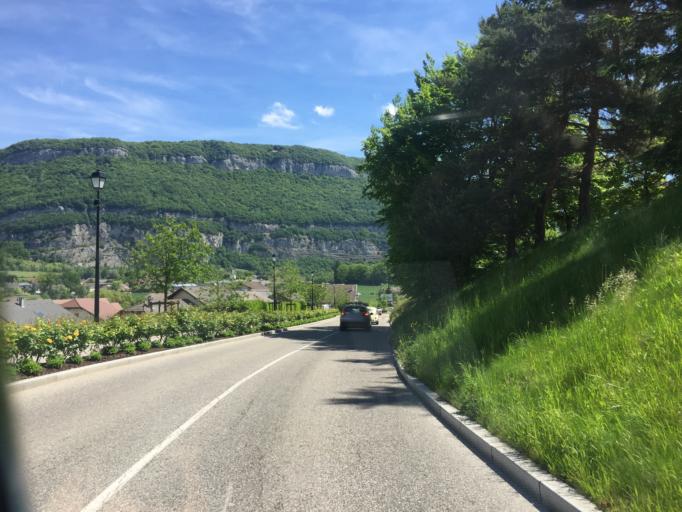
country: FR
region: Rhone-Alpes
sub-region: Departement de la Haute-Savoie
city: Sillingy
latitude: 45.9470
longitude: 6.0355
